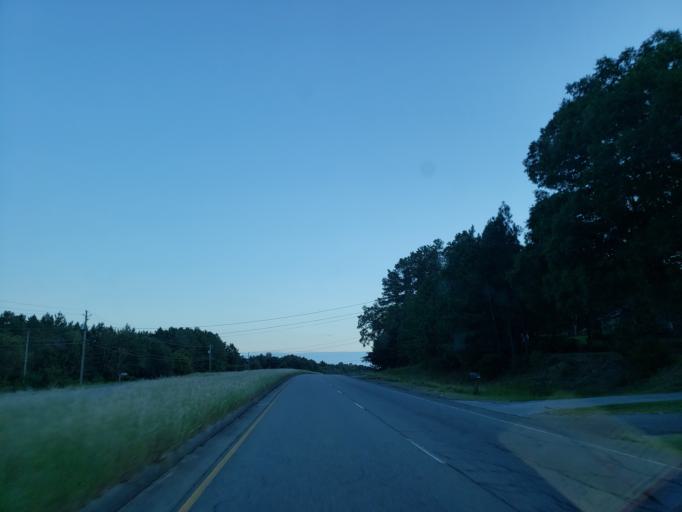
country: US
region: Georgia
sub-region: Polk County
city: Cedartown
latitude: 34.0612
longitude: -85.2325
